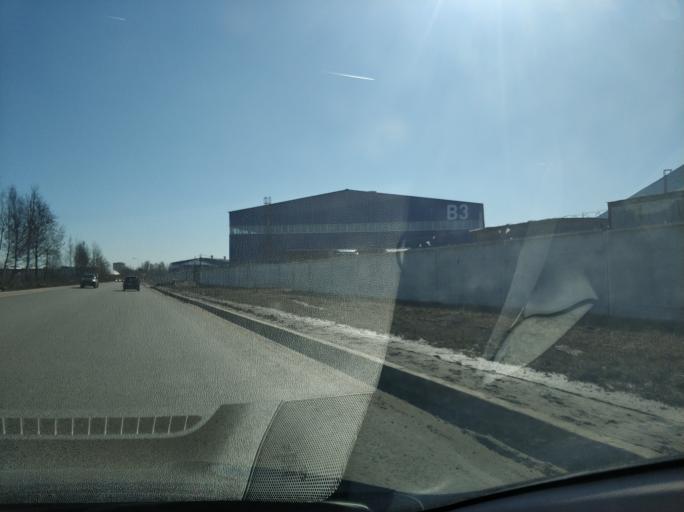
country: RU
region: Leningrad
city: Bugry
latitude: 60.0639
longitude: 30.3839
